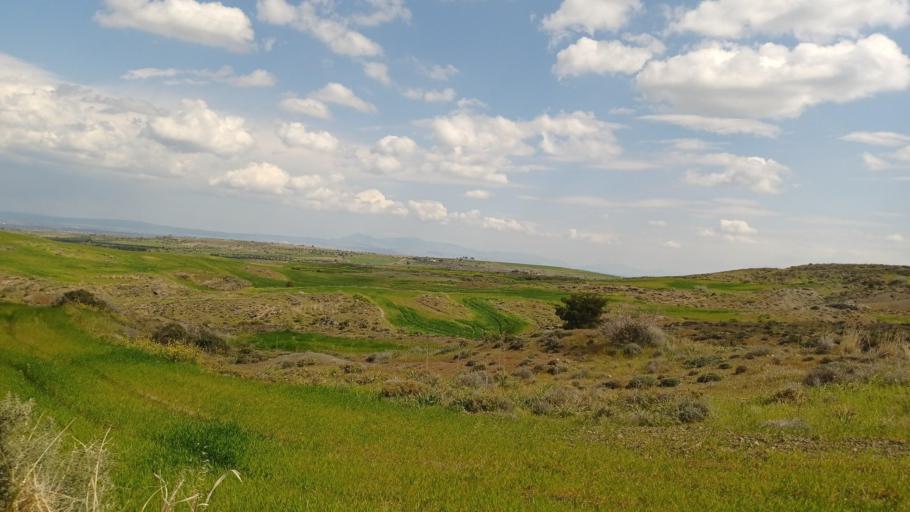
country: CY
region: Lefkosia
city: Lefka
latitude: 35.0812
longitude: 32.9066
